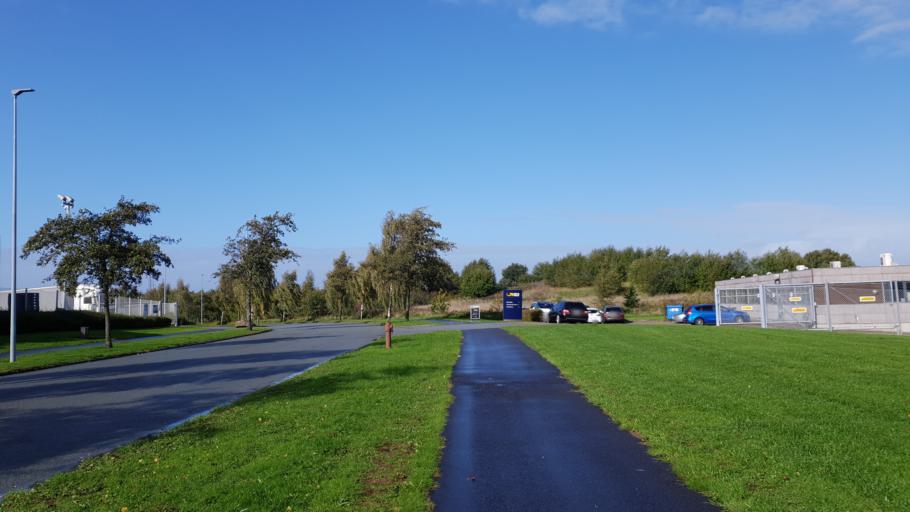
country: DK
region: South Denmark
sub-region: Kolding Kommune
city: Kolding
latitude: 55.5353
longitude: 9.4777
